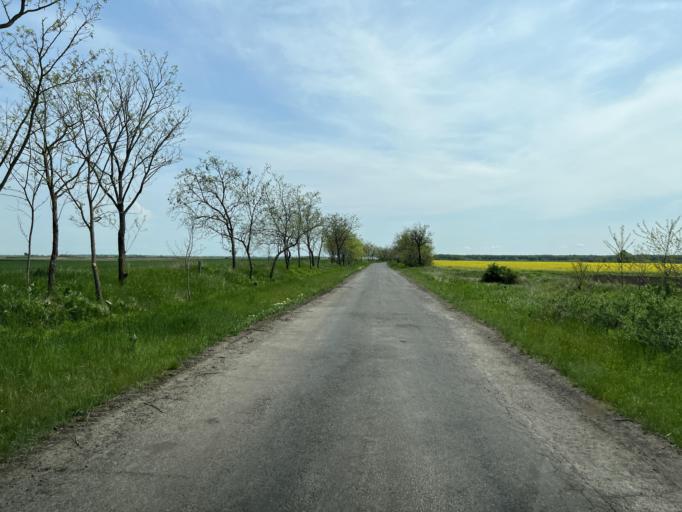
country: HU
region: Pest
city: Tapiogyorgye
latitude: 47.2976
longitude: 19.9865
